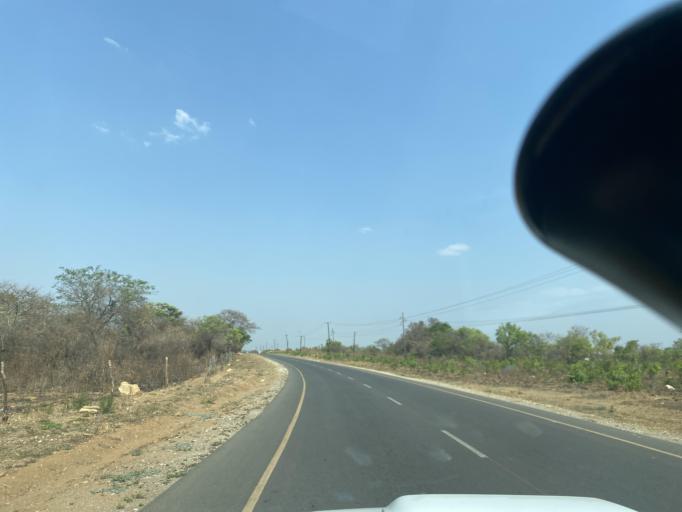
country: ZM
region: Lusaka
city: Lusaka
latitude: -15.3488
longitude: 28.0998
